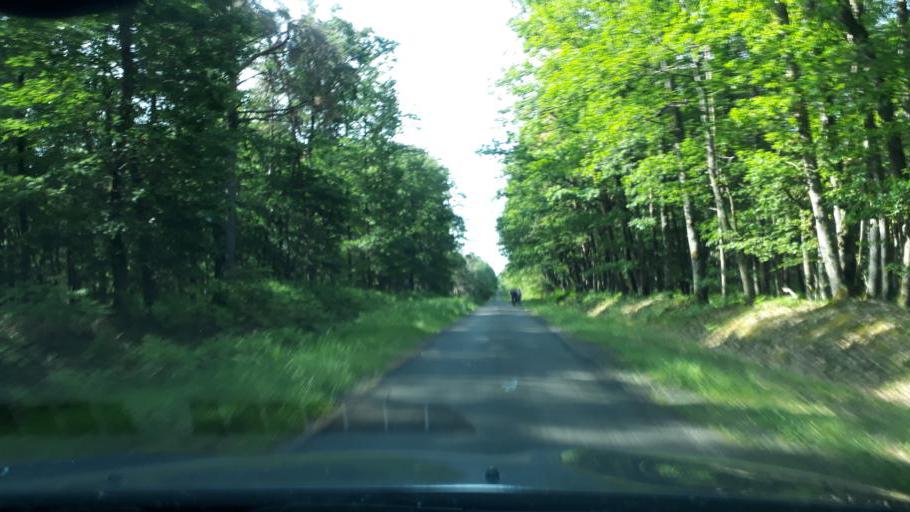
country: FR
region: Centre
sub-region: Departement du Loiret
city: Vitry-aux-Loges
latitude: 48.0343
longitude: 2.2582
